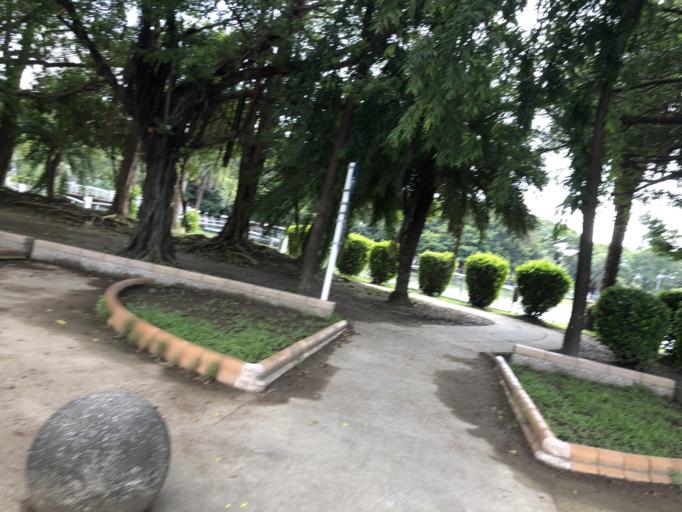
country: TW
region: Kaohsiung
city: Kaohsiung
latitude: 22.6795
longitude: 120.2966
